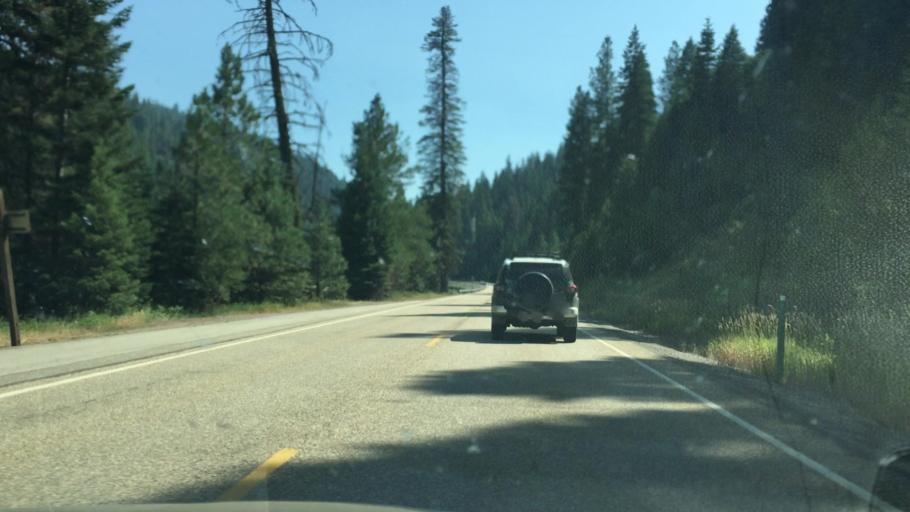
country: US
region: Idaho
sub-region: Valley County
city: Cascade
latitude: 44.2196
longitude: -116.1073
